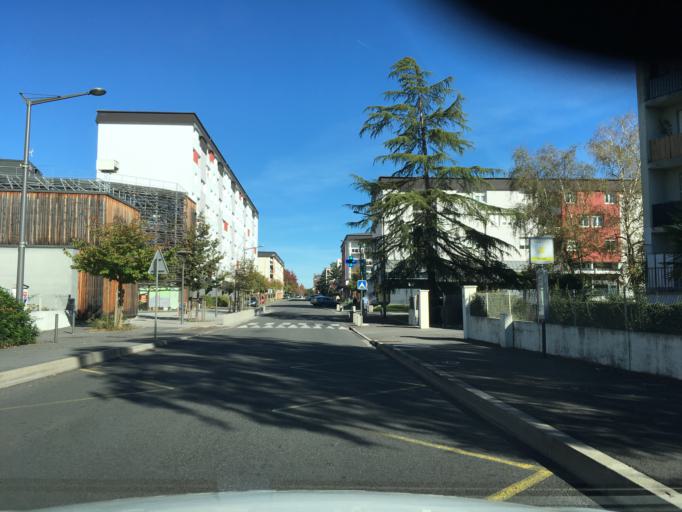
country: FR
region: Aquitaine
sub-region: Departement des Pyrenees-Atlantiques
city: Pau
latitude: 43.3134
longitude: -0.3453
